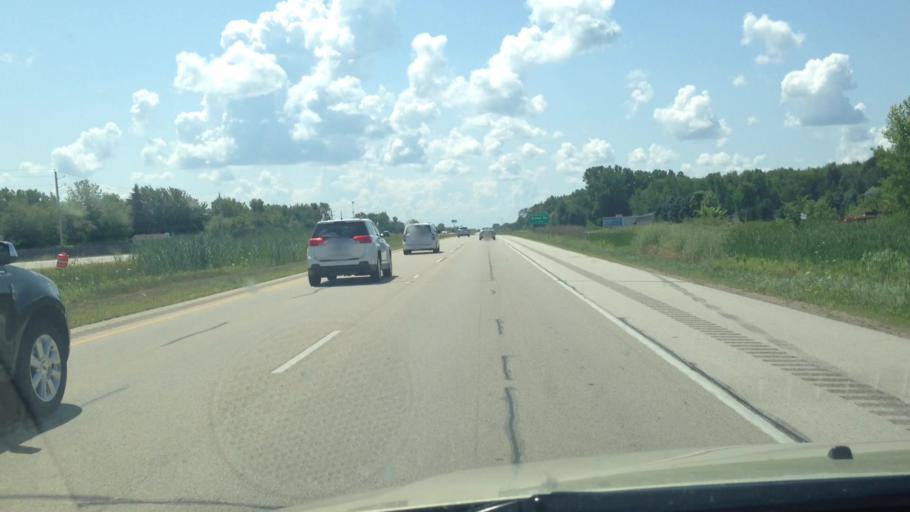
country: US
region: Wisconsin
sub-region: Brown County
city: Suamico
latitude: 44.6986
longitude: -88.0509
